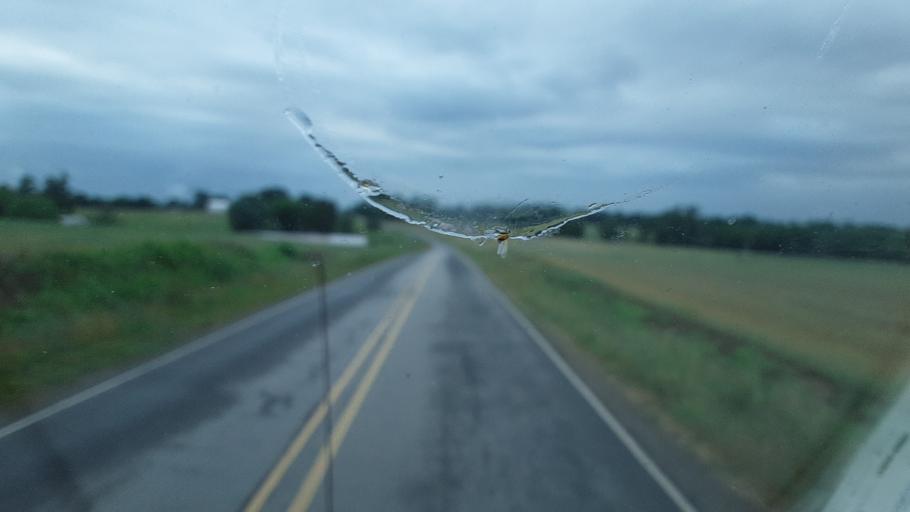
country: US
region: North Carolina
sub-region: Yadkin County
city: Jonesville
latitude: 36.0575
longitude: -80.8310
